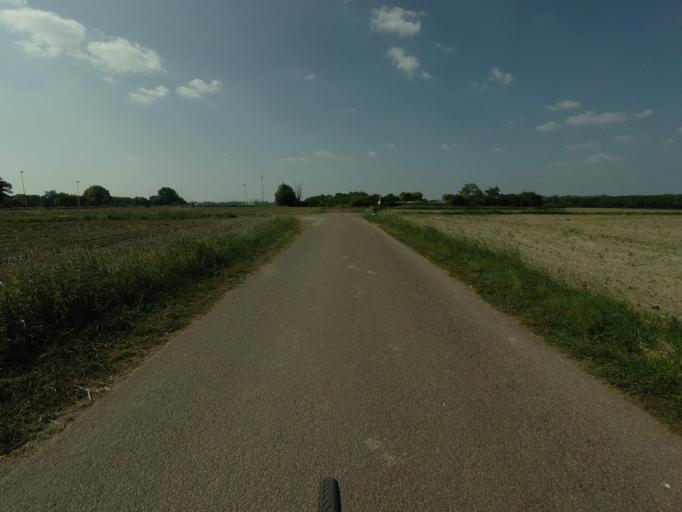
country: BE
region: Flanders
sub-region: Provincie Antwerpen
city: Borsbeek
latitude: 51.1785
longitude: 4.4746
